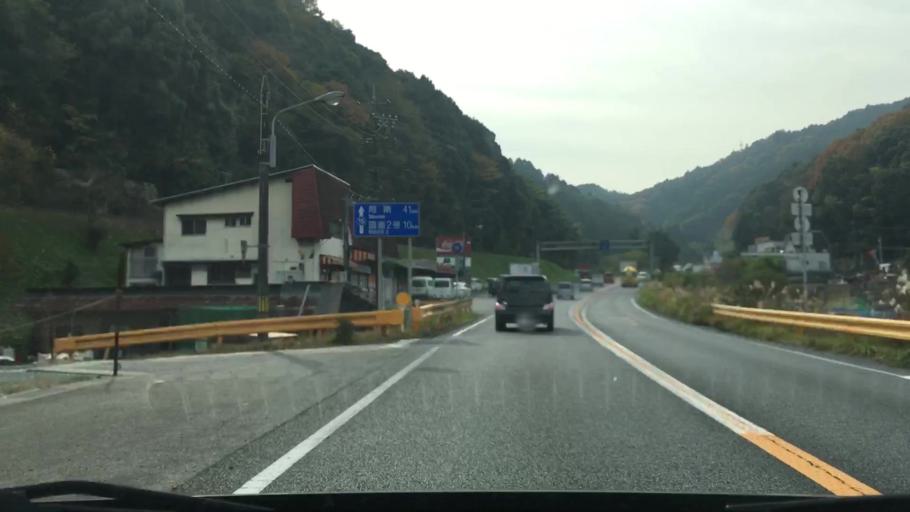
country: JP
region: Yamaguchi
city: Iwakuni
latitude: 34.1537
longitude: 132.1739
